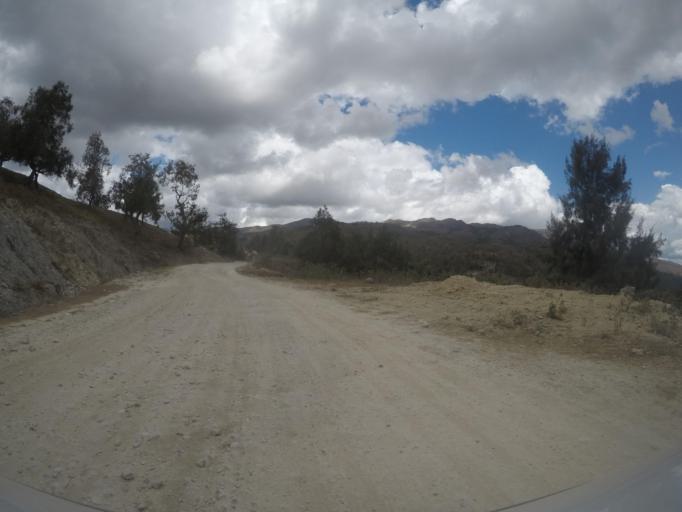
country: TL
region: Baucau
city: Baucau
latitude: -8.5002
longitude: 126.6776
